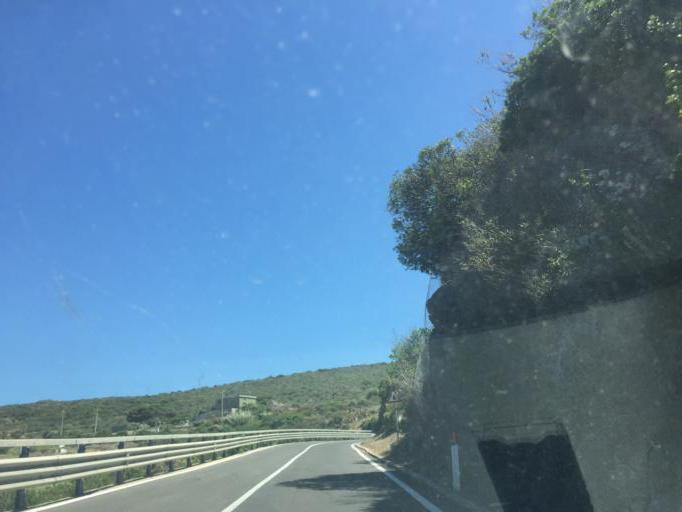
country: IT
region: Sardinia
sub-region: Provincia di Sassari
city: Castelsardo
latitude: 40.9111
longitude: 8.7293
